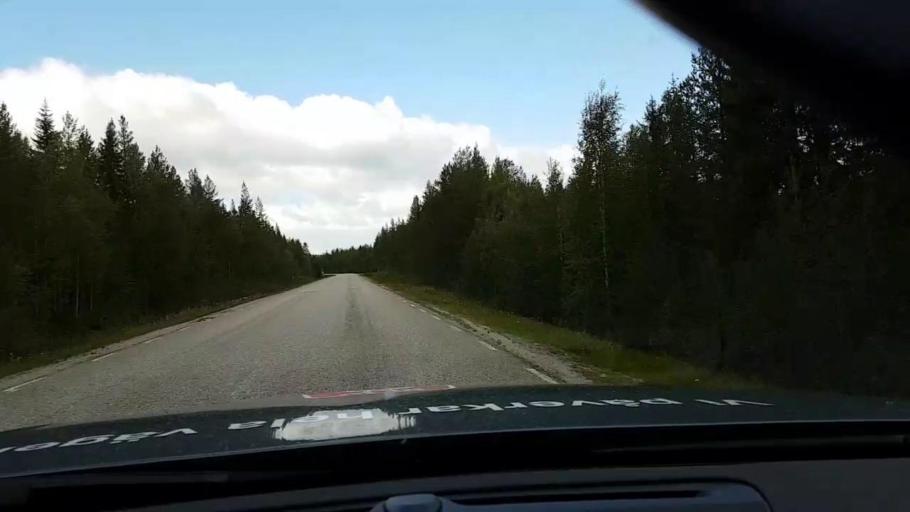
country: SE
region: Vaesterbotten
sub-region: Asele Kommun
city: Asele
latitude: 63.9229
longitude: 17.3201
